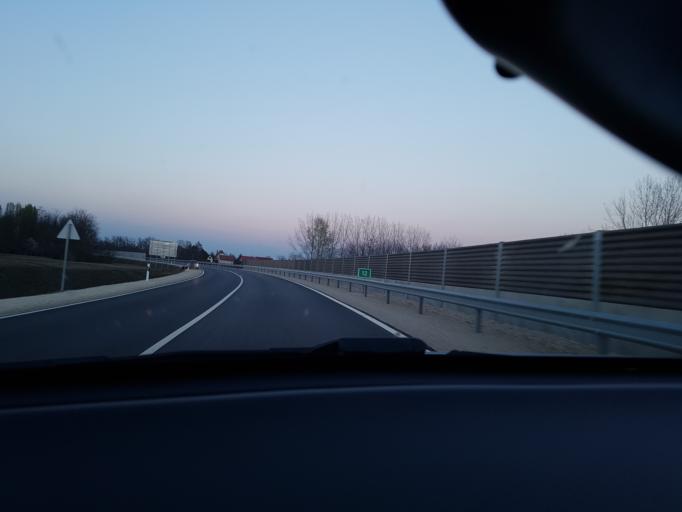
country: HU
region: Bacs-Kiskun
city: Kecskemet
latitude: 46.9312
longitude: 19.6348
